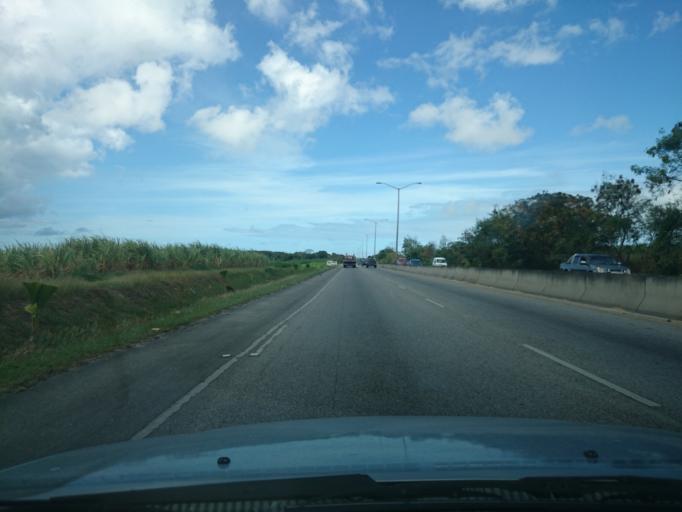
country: BB
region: Saint Michael
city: Bridgetown
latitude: 13.1209
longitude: -59.5901
